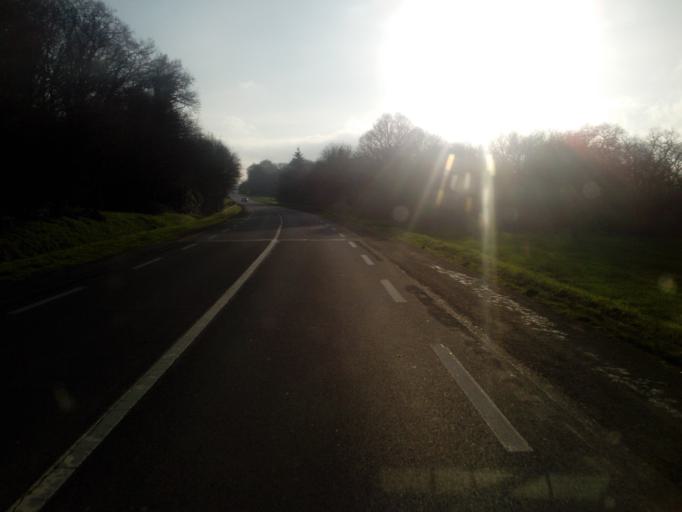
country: FR
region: Brittany
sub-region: Departement du Morbihan
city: Loyat
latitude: 47.9733
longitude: -2.3822
